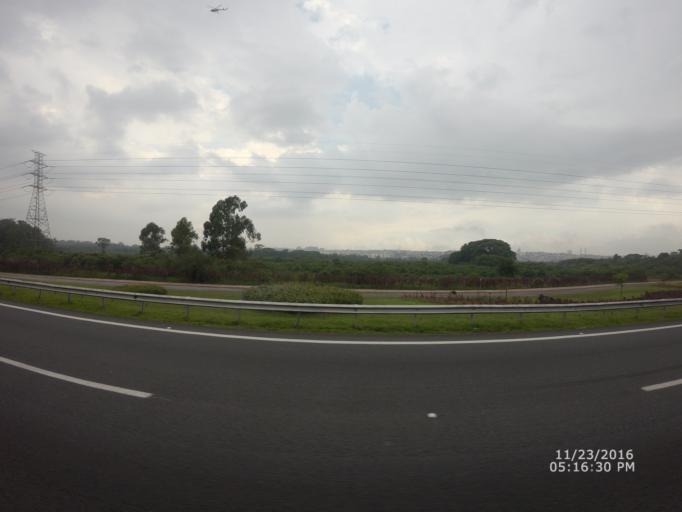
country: BR
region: Sao Paulo
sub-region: Guarulhos
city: Guarulhos
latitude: -23.4897
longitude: -46.5343
